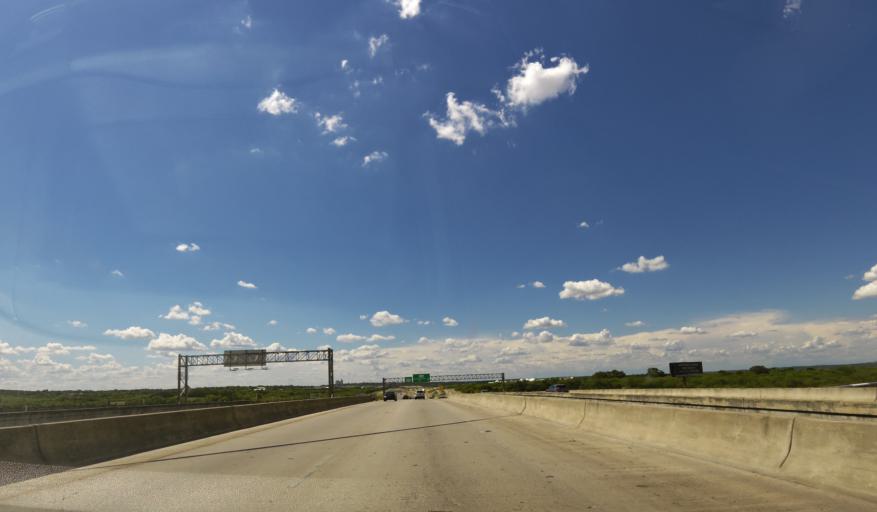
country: US
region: Texas
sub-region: Bexar County
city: Live Oak
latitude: 29.5815
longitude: -98.3447
